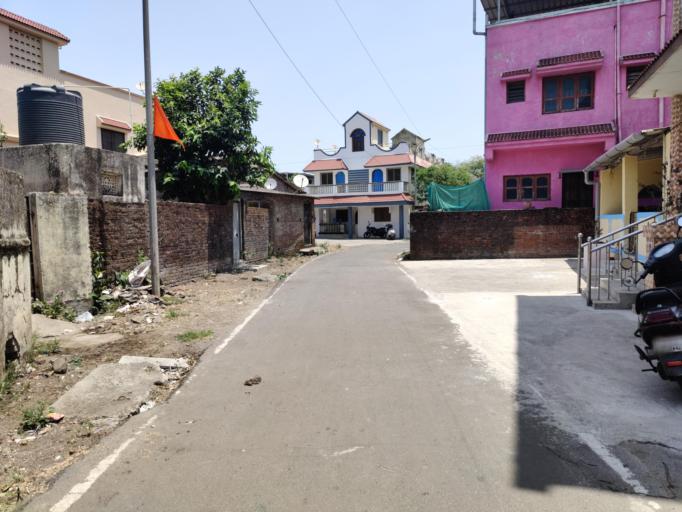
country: IN
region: Daman and Diu
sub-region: Daman District
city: Daman
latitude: 20.4054
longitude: 72.8297
